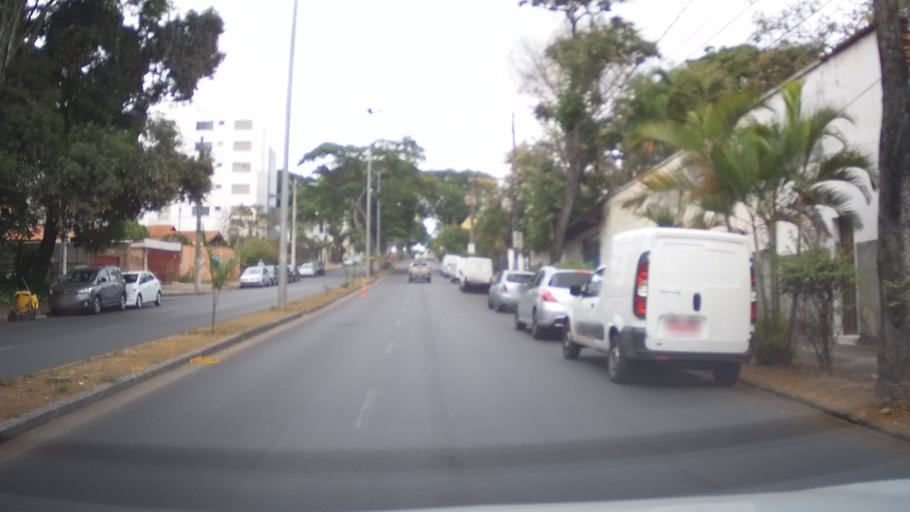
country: BR
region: Minas Gerais
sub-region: Belo Horizonte
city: Belo Horizonte
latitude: -19.8514
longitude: -43.9588
